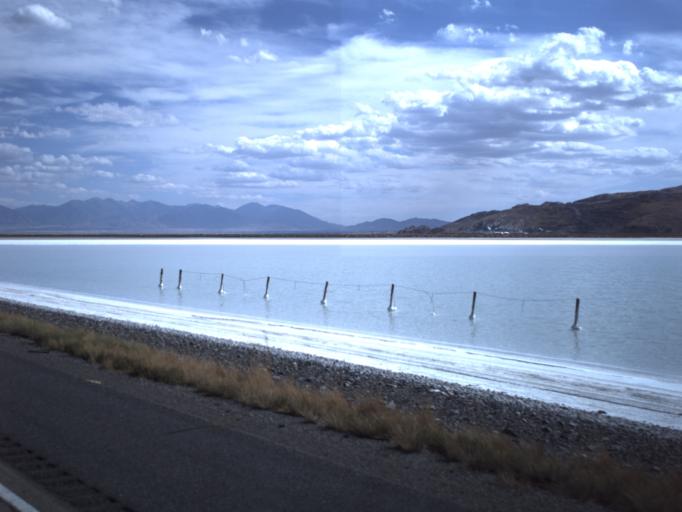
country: US
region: Utah
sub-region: Tooele County
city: Grantsville
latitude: 40.7302
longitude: -112.5901
